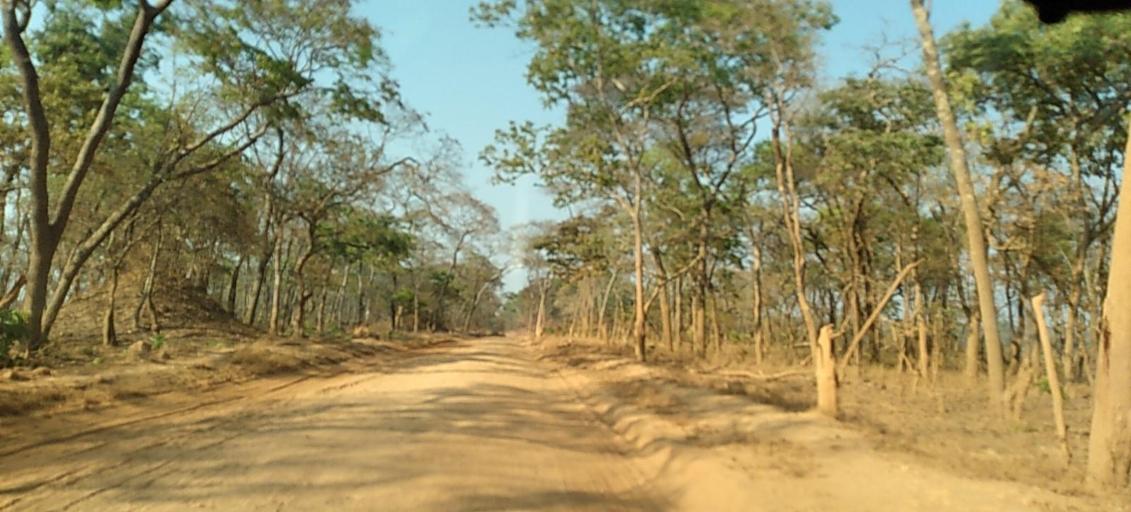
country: ZM
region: North-Western
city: Kasempa
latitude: -13.5912
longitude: 25.9837
